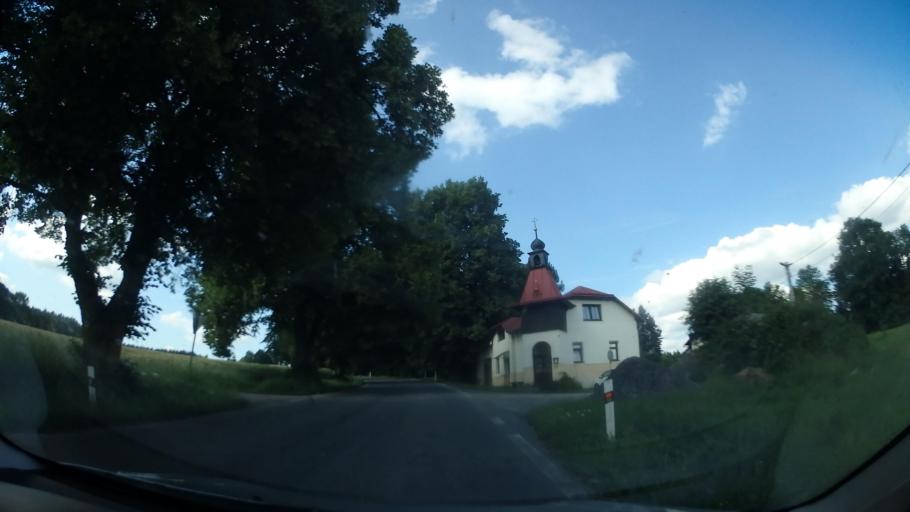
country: CZ
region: Vysocina
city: Heralec
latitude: 49.6472
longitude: 15.9689
